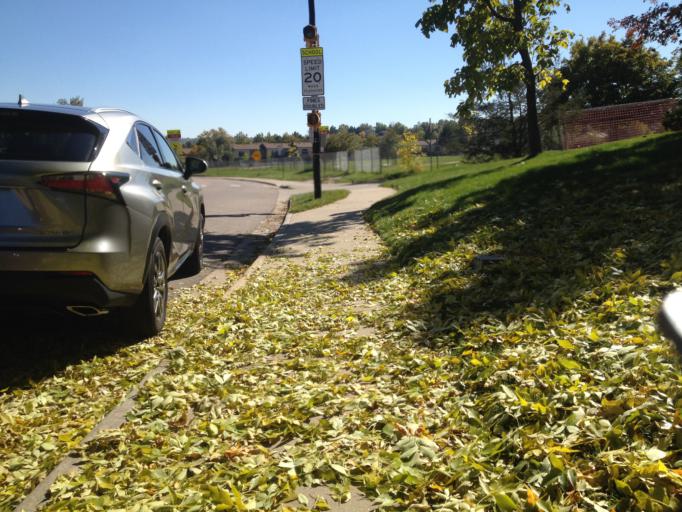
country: US
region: Colorado
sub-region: Boulder County
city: Boulder
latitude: 39.9841
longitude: -105.2396
